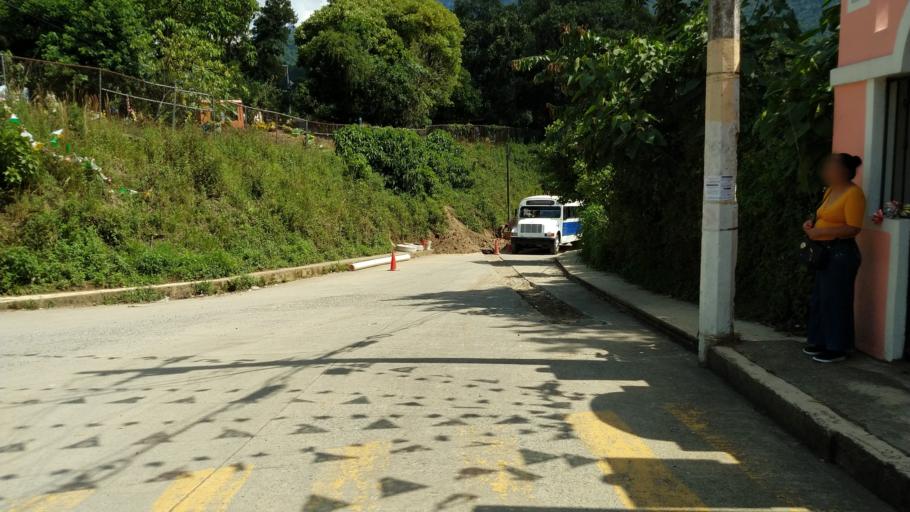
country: MX
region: Veracruz
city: Jalapilla
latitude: 18.8155
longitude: -97.0668
